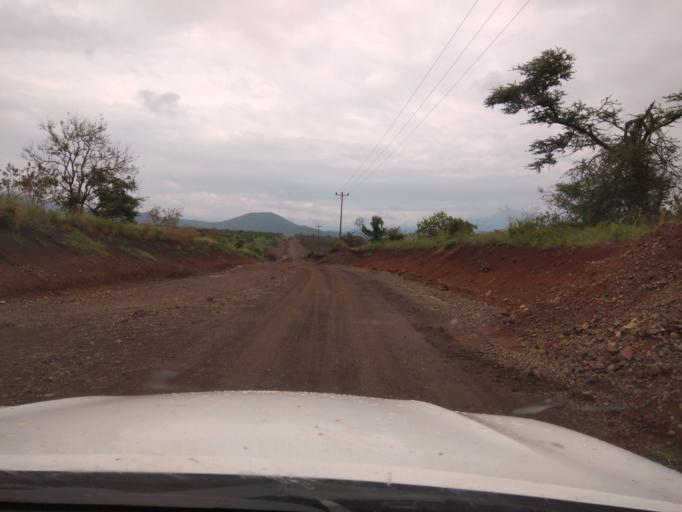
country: ET
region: Southern Nations, Nationalities, and People's Region
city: Felege Neway
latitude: 6.4273
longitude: 37.2574
